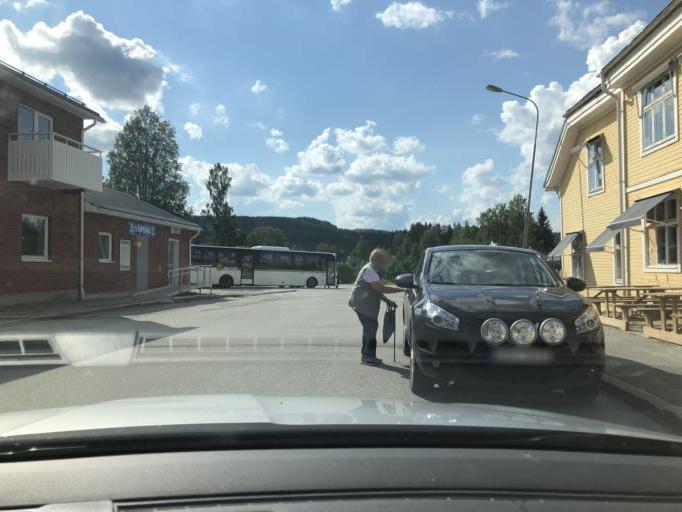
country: SE
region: Vaesternorrland
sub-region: OErnskoeldsviks Kommun
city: Bredbyn
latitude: 63.4493
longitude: 18.1075
